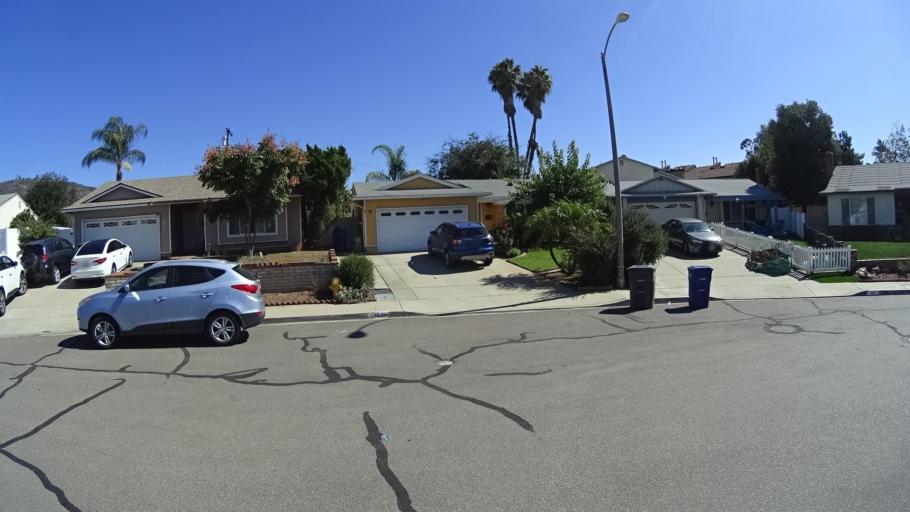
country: US
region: California
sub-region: San Diego County
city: Santee
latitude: 32.8219
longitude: -116.9571
